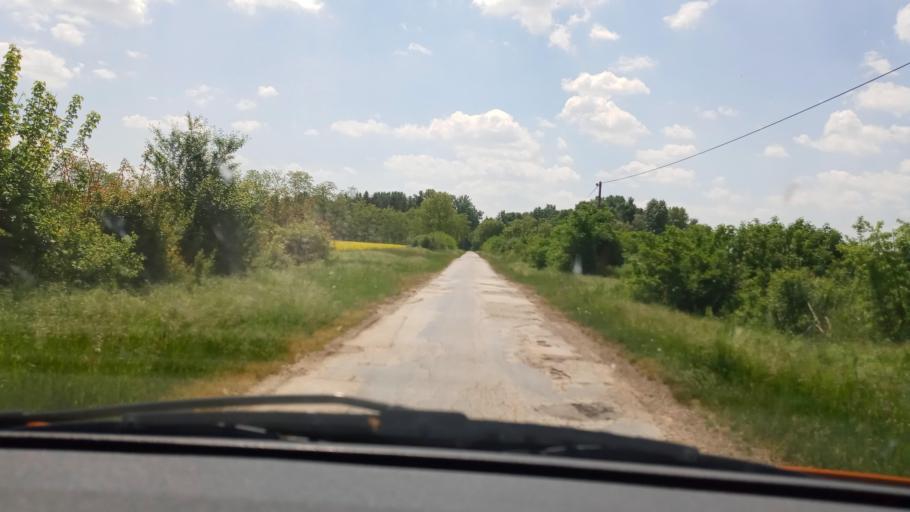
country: HU
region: Baranya
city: Siklos
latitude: 45.7751
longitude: 18.2755
